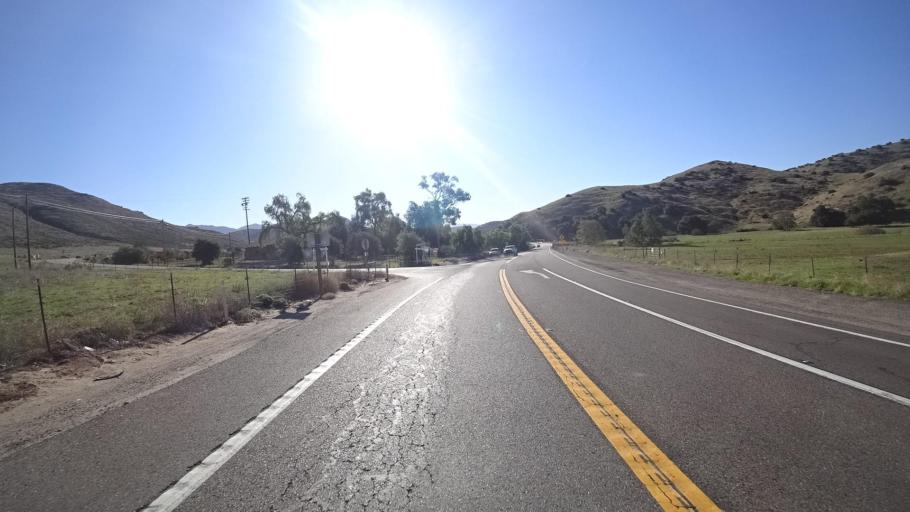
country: US
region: California
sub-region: San Diego County
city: Jamul
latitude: 32.6699
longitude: -116.8255
